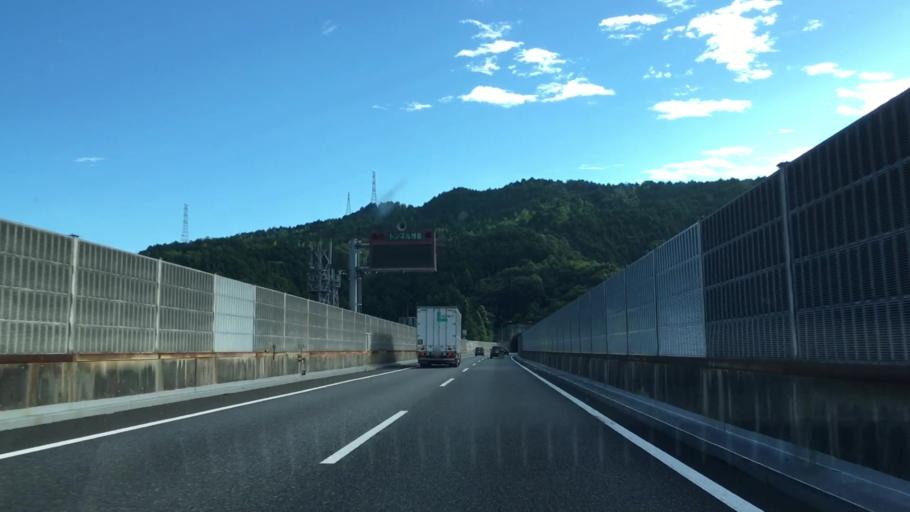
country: JP
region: Yamaguchi
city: Iwakuni
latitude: 34.1585
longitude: 132.1515
